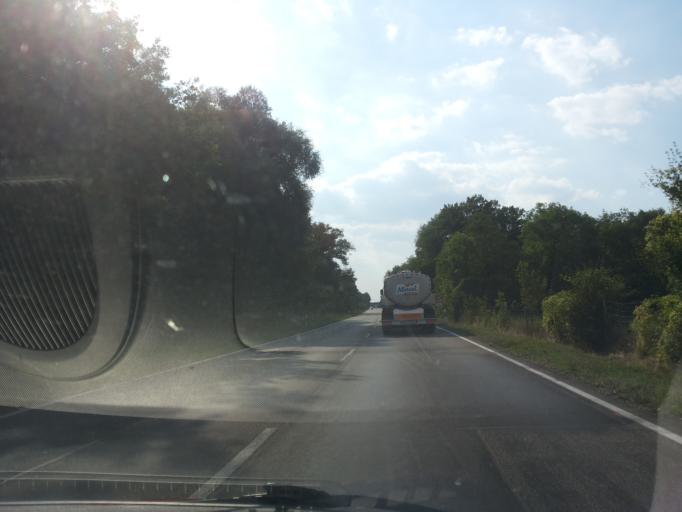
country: DE
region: Bavaria
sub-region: Upper Bavaria
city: Weichering
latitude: 48.7167
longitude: 11.2981
